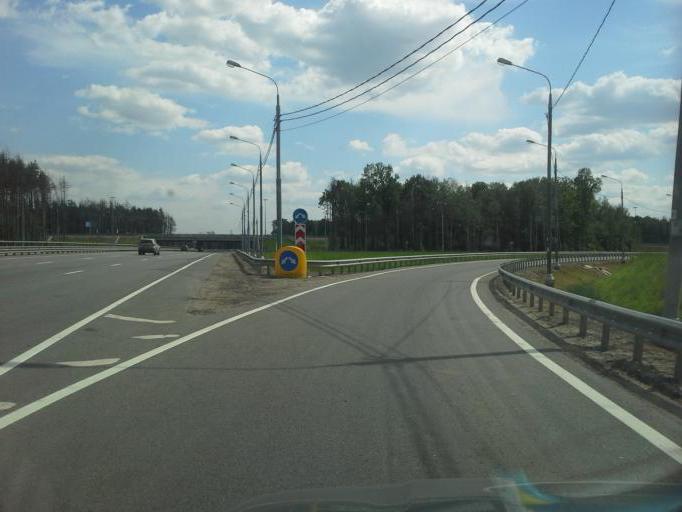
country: RU
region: Moskovskaya
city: Odintsovo
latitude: 55.6961
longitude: 37.2697
